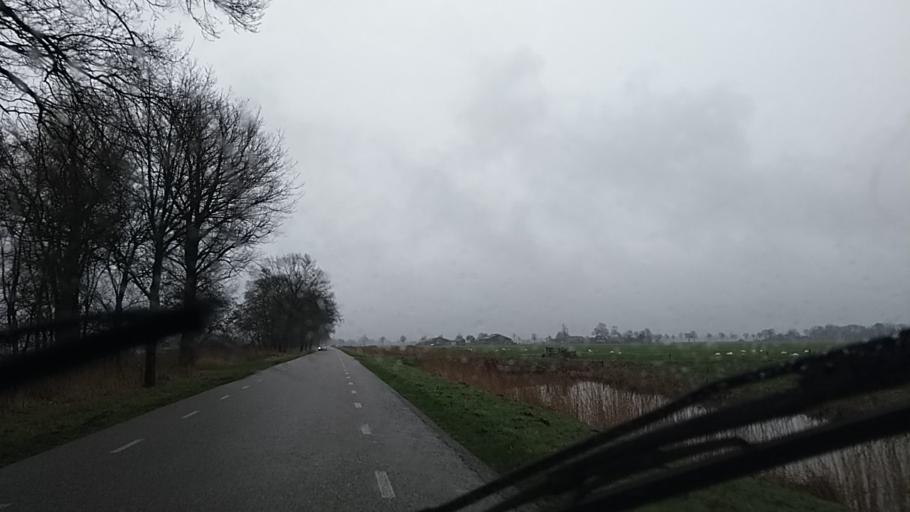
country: NL
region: Overijssel
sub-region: Gemeente Zwartewaterland
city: Hasselt
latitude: 52.6104
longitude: 6.1503
